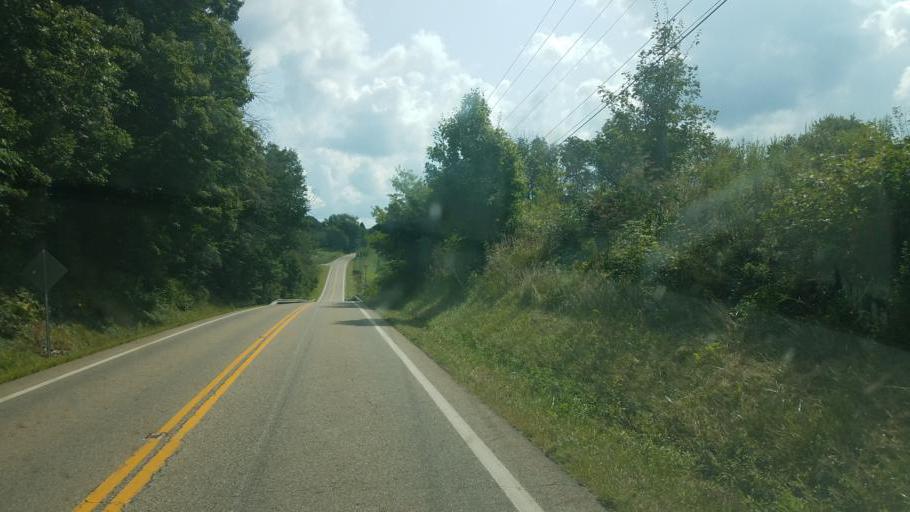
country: US
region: Ohio
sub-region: Columbiana County
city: Lisbon
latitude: 40.7843
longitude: -80.8318
